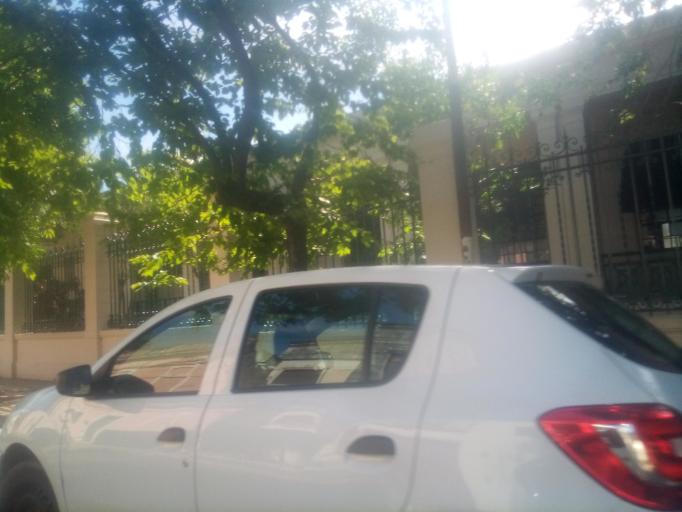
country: AR
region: Corrientes
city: Corrientes
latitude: -27.4621
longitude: -58.8413
